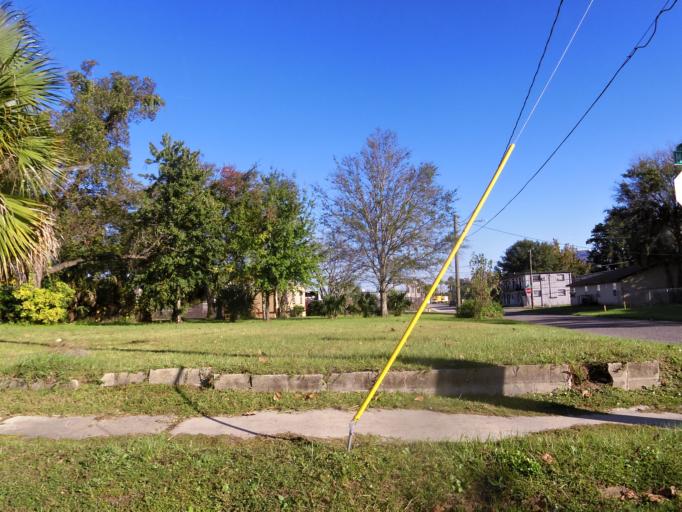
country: US
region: Florida
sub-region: Duval County
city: Jacksonville
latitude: 30.3369
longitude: -81.6739
